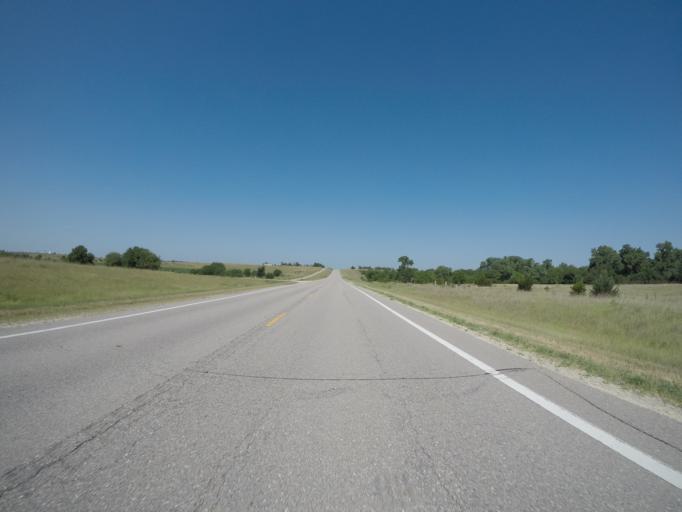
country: US
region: Kansas
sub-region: Clay County
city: Clay Center
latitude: 39.3648
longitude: -97.4301
